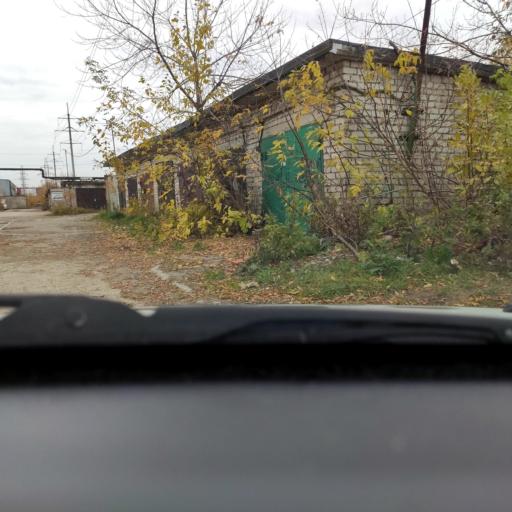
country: RU
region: Perm
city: Perm
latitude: 57.9663
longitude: 56.2475
